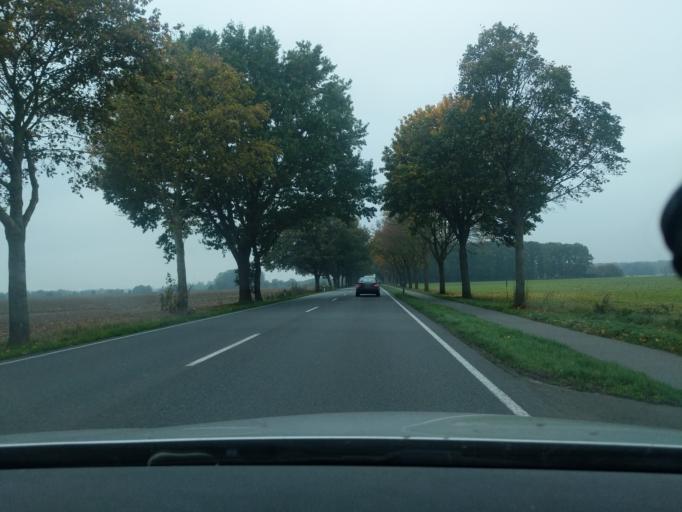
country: DE
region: Lower Saxony
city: Dudenbuttel
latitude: 53.5931
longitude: 9.3389
